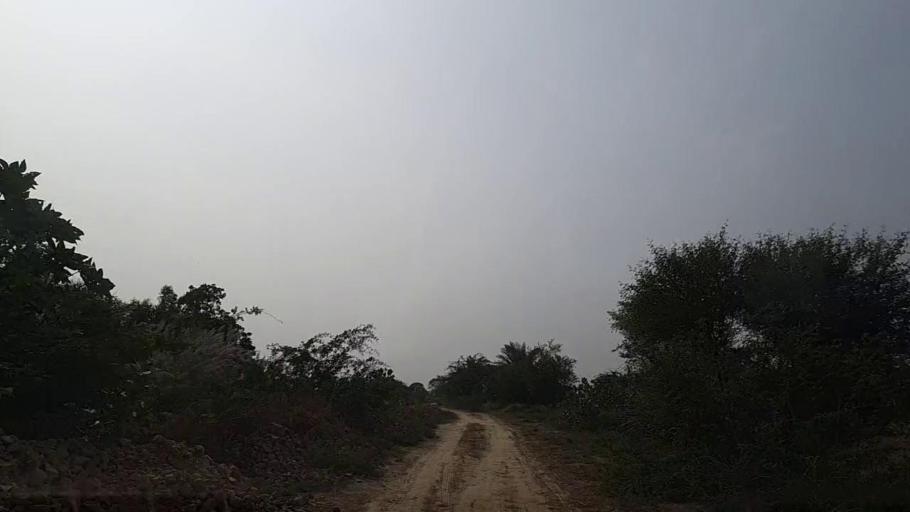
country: PK
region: Sindh
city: Thatta
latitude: 24.6609
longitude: 67.7721
